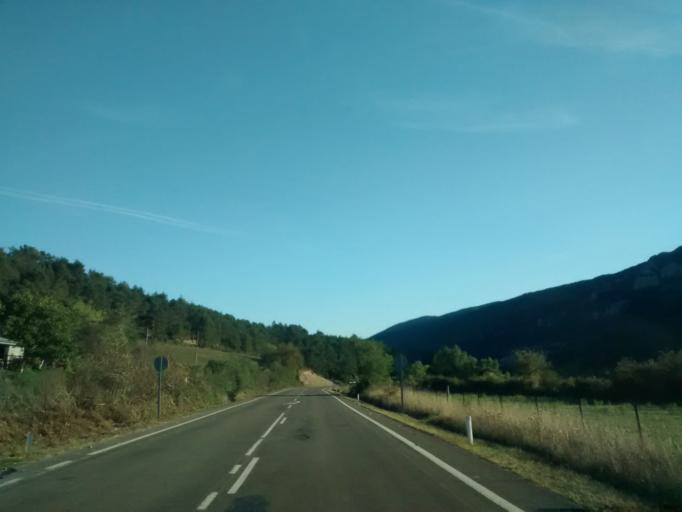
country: ES
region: Aragon
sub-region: Provincia de Huesca
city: Aragues del Puerto
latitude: 42.7228
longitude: -0.7516
